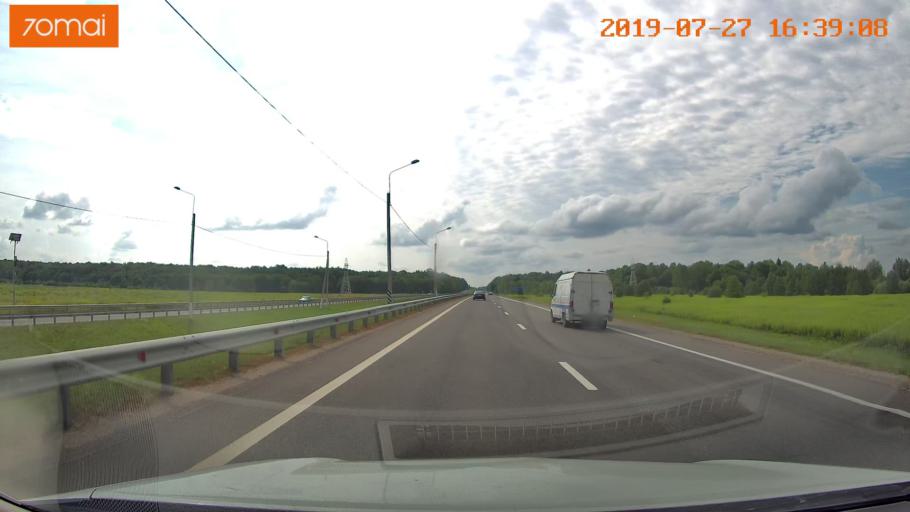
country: RU
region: Kaliningrad
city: Gvardeysk
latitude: 54.6492
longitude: 21.2088
